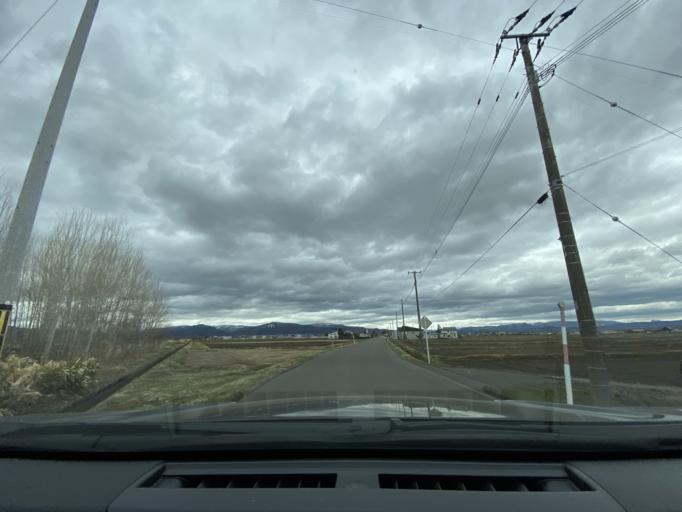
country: JP
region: Hokkaido
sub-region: Asahikawa-shi
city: Asahikawa
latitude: 43.8633
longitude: 142.4694
